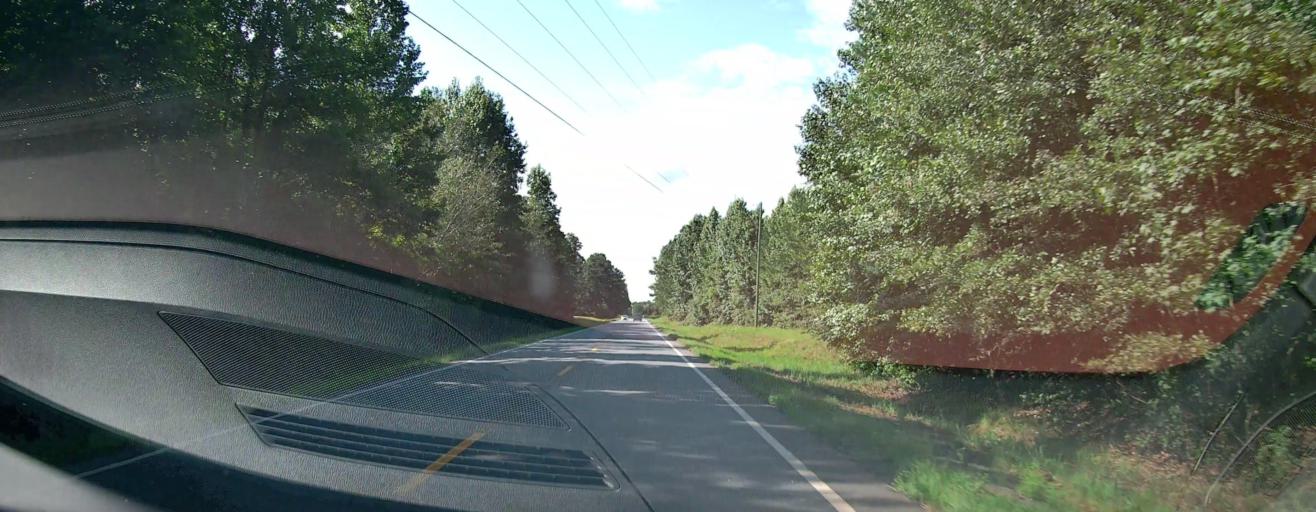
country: US
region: Georgia
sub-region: Upson County
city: Hannahs Mill
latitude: 32.9563
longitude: -84.4616
